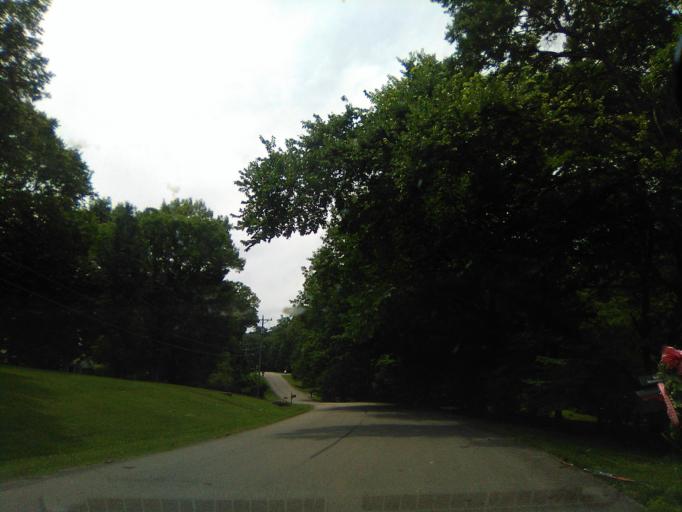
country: US
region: Tennessee
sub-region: Davidson County
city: Belle Meade
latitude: 36.1136
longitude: -86.8950
